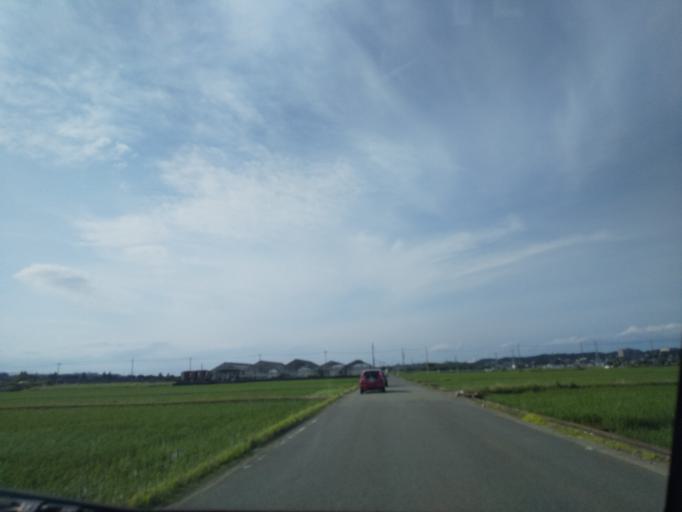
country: JP
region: Kanagawa
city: Zama
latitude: 35.4813
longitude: 139.3815
